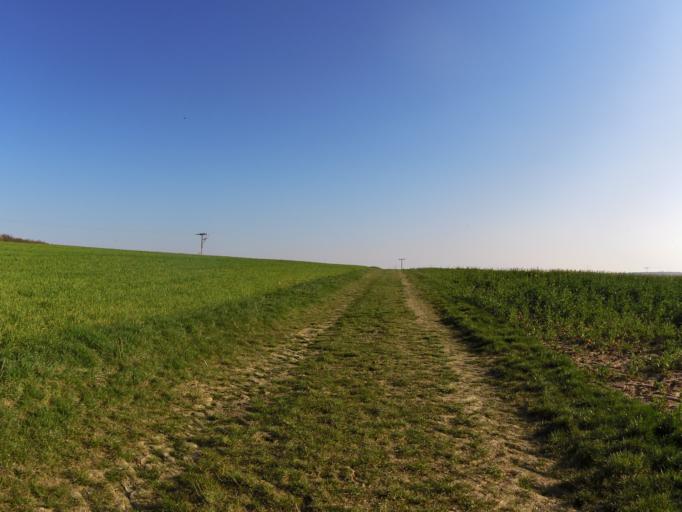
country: DE
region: Bavaria
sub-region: Regierungsbezirk Unterfranken
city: Rottendorf
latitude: 49.8216
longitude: 10.0558
